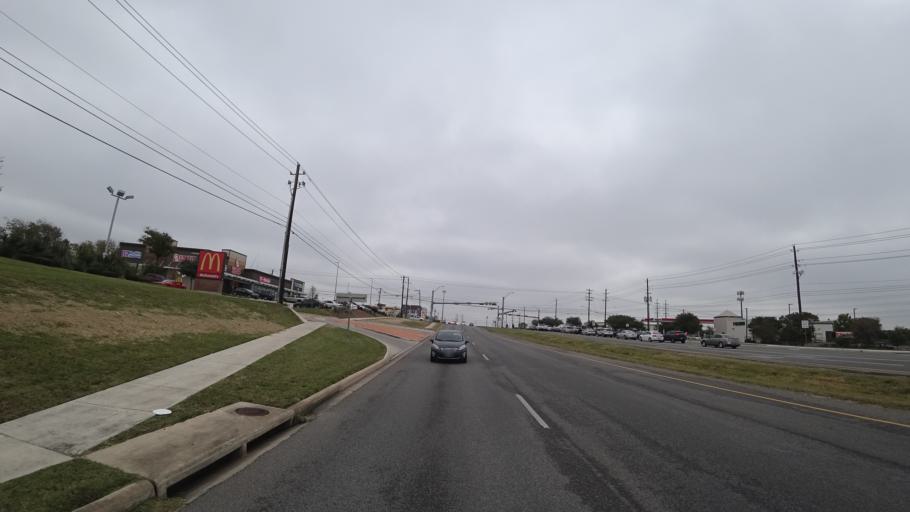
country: US
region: Texas
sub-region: Travis County
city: Pflugerville
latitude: 30.3878
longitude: -97.6496
